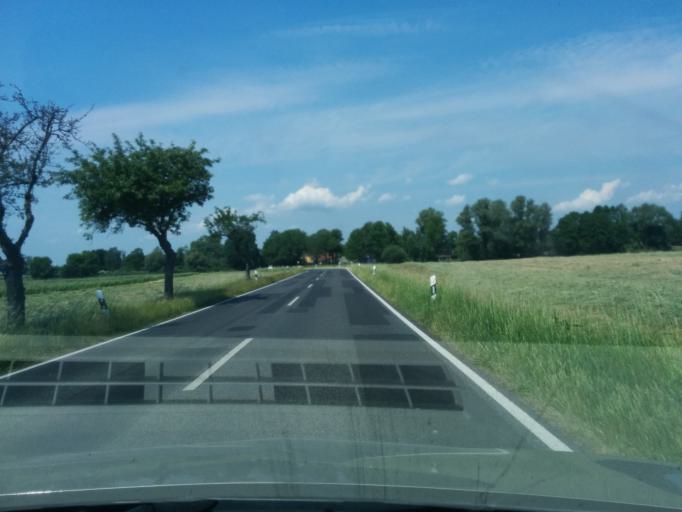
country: DE
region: Brandenburg
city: Ahrensfelde
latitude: 52.6221
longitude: 13.5790
